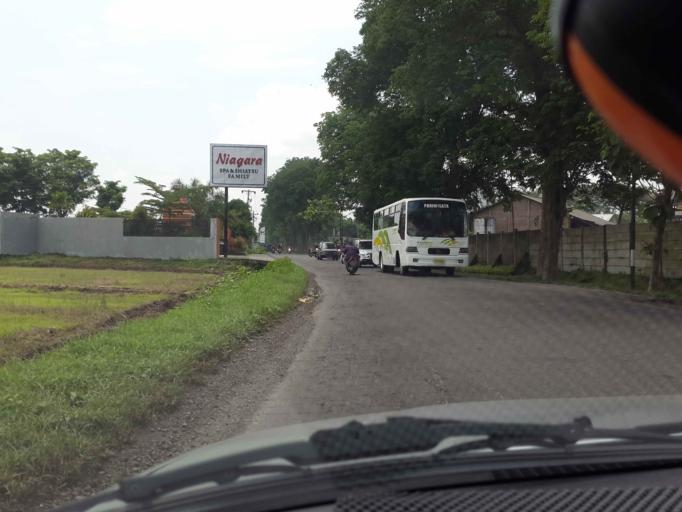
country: ID
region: Central Java
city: Ngemplak
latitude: -7.5390
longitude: 110.7230
